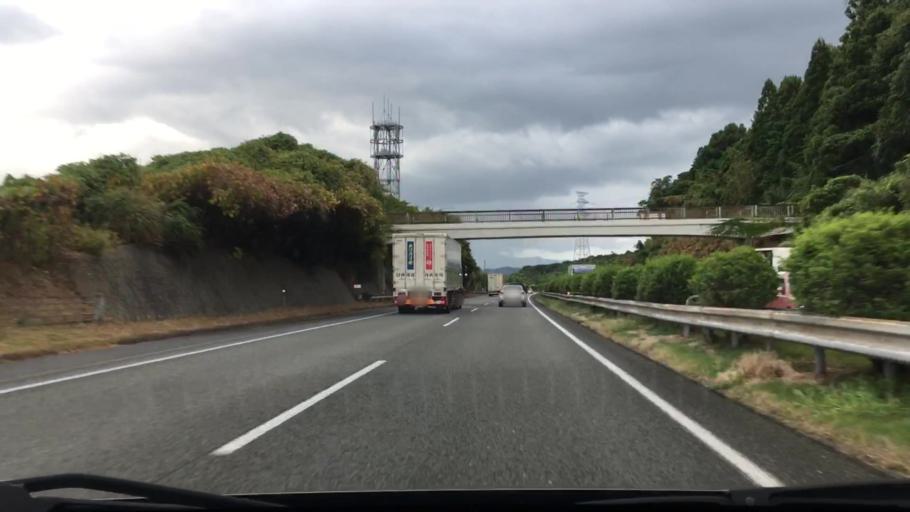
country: JP
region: Fukuoka
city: Miyata
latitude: 33.7502
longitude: 130.5857
